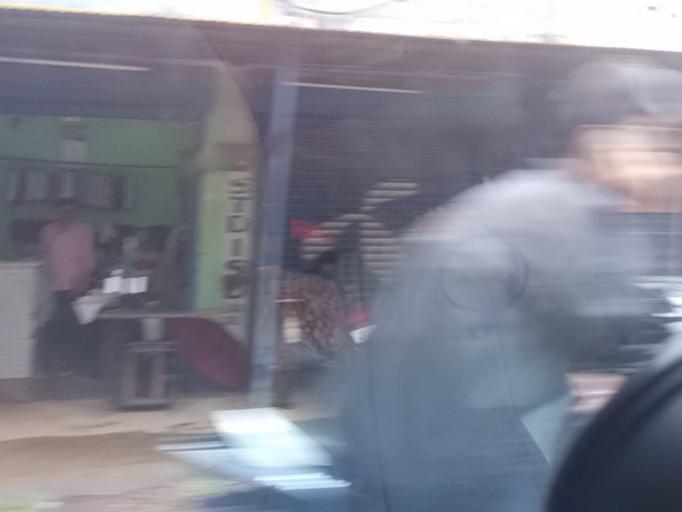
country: IN
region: Kerala
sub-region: Kozhikode
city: Kozhikode
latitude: 11.2772
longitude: 75.8104
